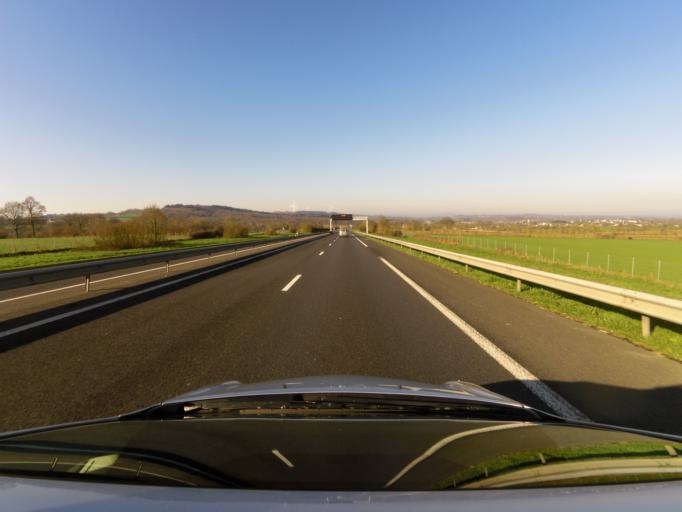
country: FR
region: Lower Normandy
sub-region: Departement de la Manche
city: Saint-Amand
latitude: 48.9897
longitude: -0.9267
